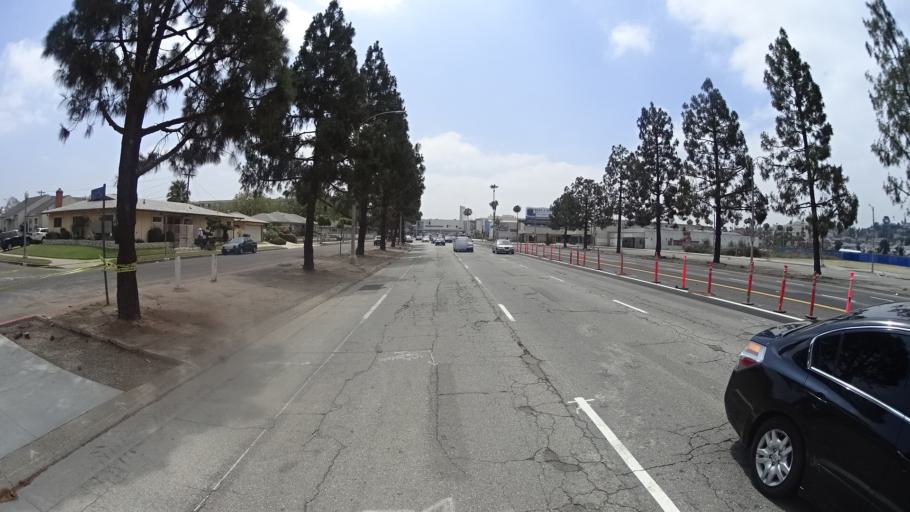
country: US
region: California
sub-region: Los Angeles County
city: View Park-Windsor Hills
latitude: 34.0134
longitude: -118.3393
